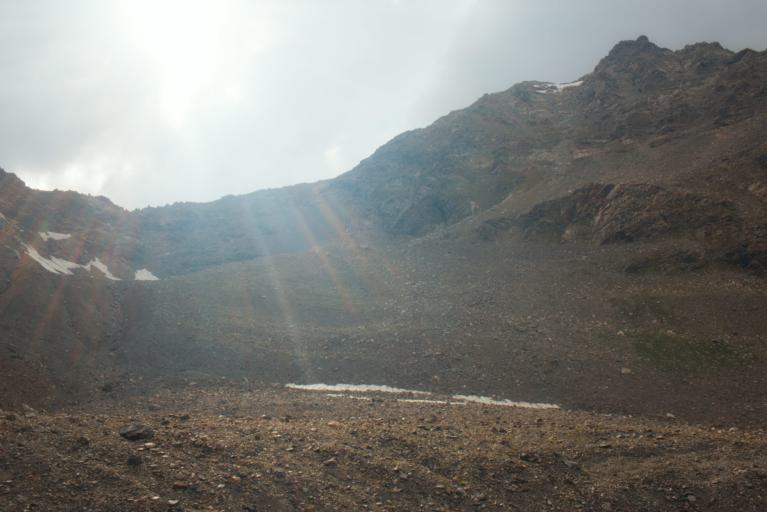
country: RU
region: Karachayevo-Cherkesiya
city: Nizhniy Arkhyz
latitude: 43.4255
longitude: 41.2506
